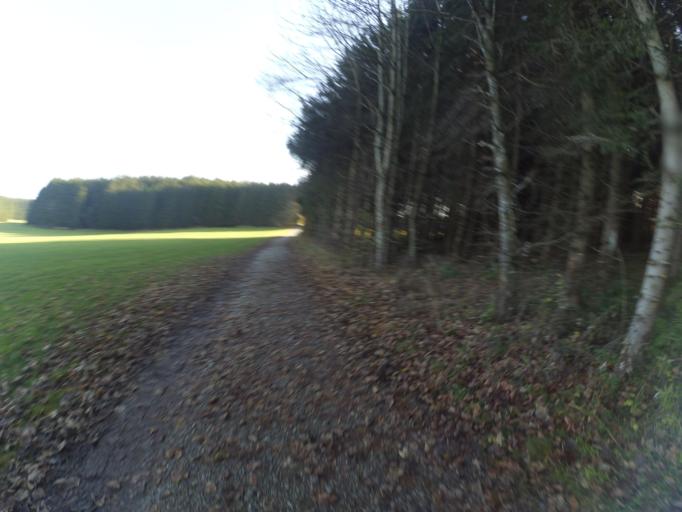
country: DE
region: Bavaria
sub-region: Swabia
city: Ruderatshofen
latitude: 47.8062
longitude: 10.5614
